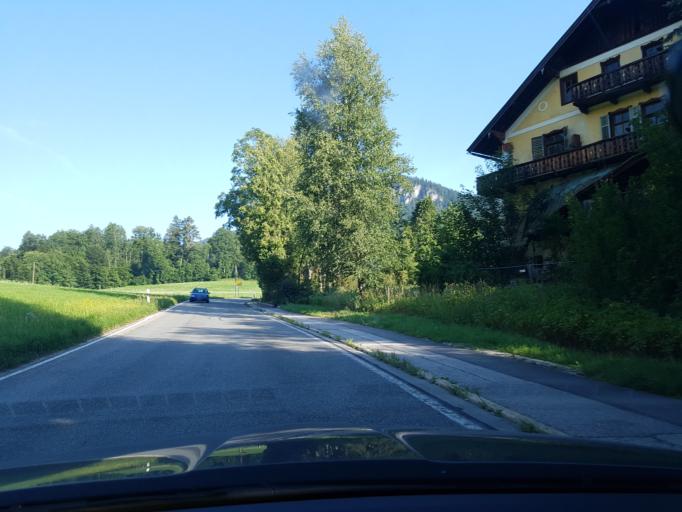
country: DE
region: Bavaria
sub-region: Upper Bavaria
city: Berchtesgaden
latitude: 47.6410
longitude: 13.0022
